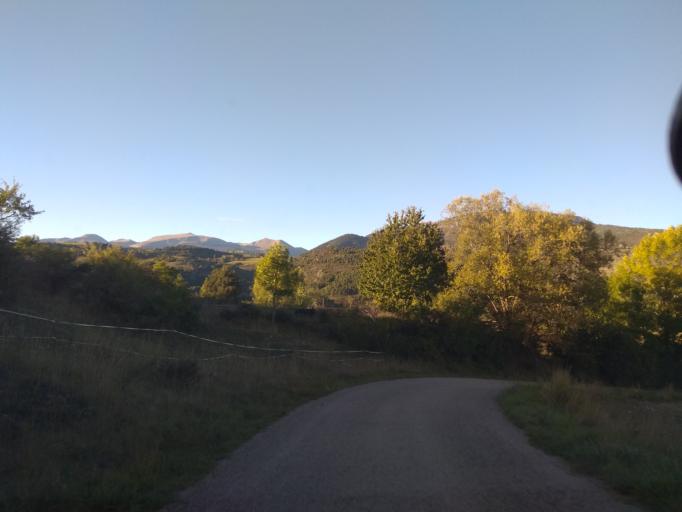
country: ES
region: Catalonia
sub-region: Provincia de Lleida
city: Lles de Cerdanya
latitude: 42.3606
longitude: 1.7256
